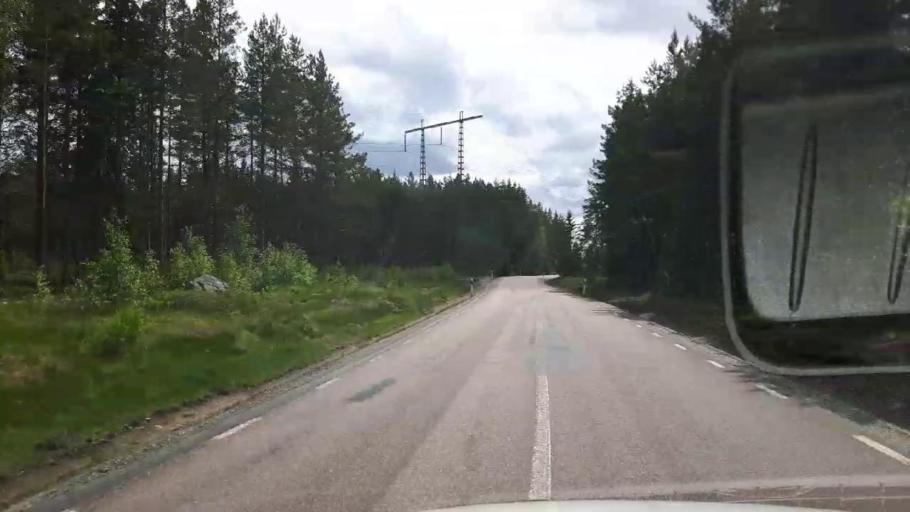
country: SE
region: Vaestmanland
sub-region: Fagersta Kommun
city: Fagersta
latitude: 59.8978
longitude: 15.8202
